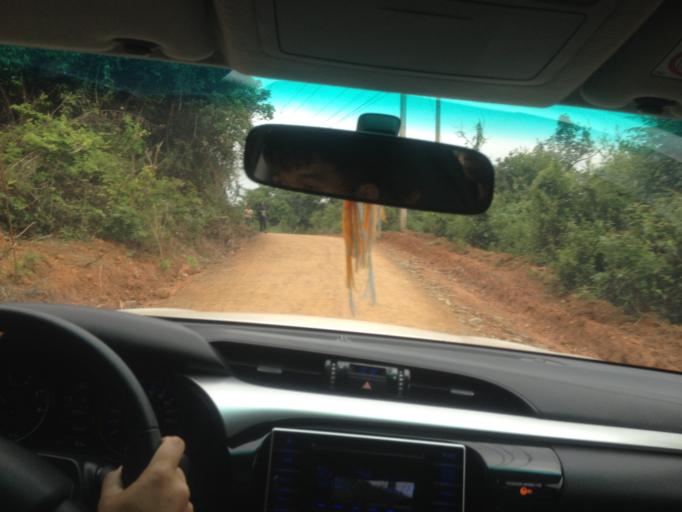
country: TH
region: Nan
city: Chaloem Phra Kiat
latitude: 19.9689
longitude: 101.1369
